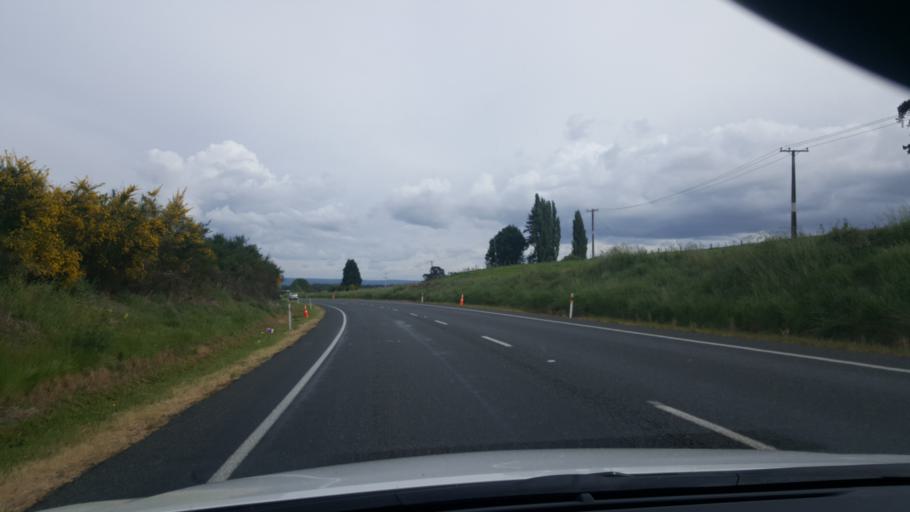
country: NZ
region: Bay of Plenty
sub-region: Rotorua District
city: Rotorua
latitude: -38.4454
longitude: 176.3140
